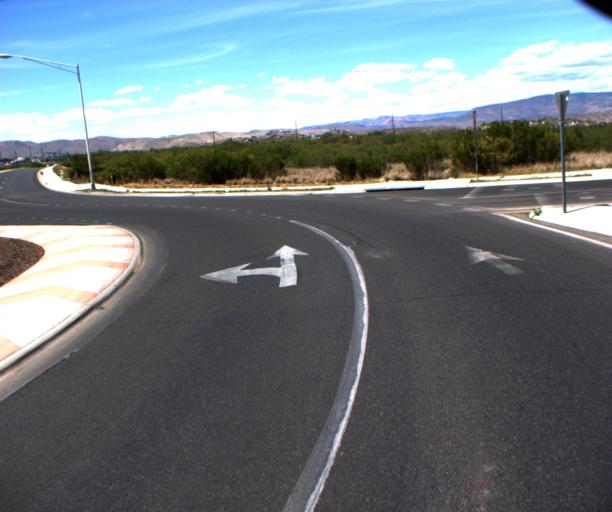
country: US
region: Arizona
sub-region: Yavapai County
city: Cottonwood
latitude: 34.7400
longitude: -112.0371
